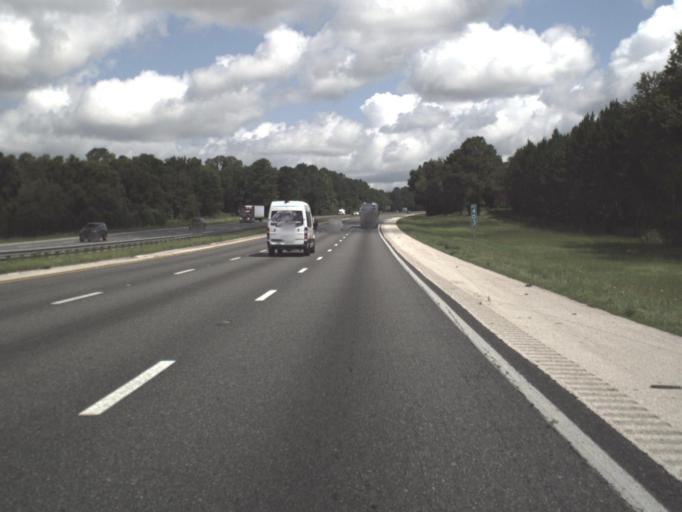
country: US
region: Florida
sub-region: Alachua County
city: High Springs
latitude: 29.8552
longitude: -82.5371
